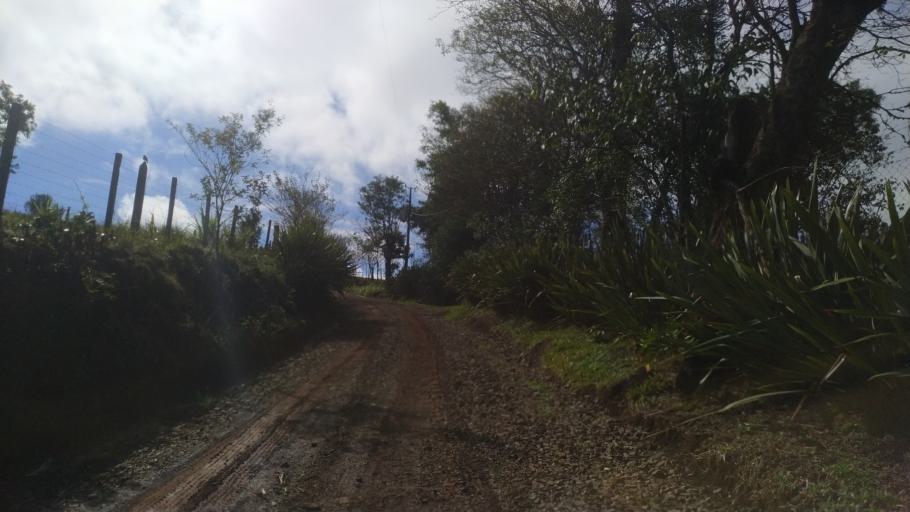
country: BR
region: Santa Catarina
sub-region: Chapeco
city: Chapeco
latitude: -27.1550
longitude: -52.5958
